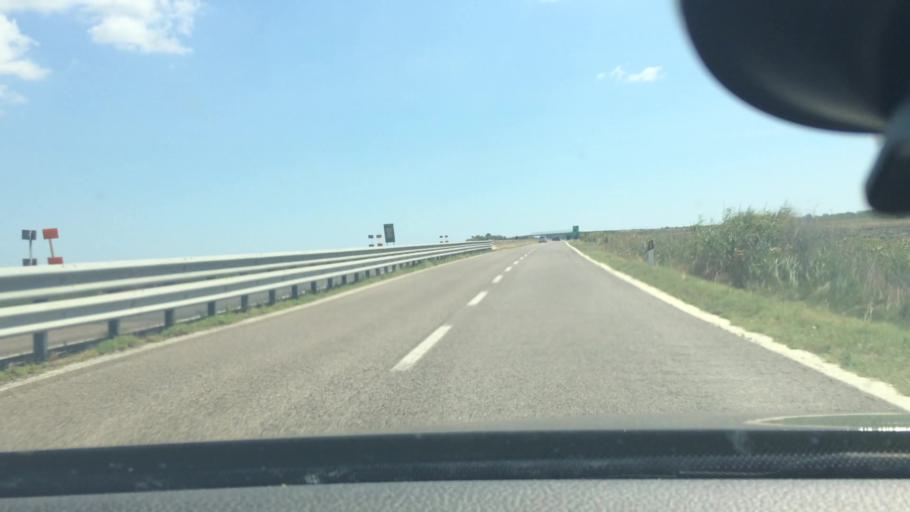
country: IT
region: Emilia-Romagna
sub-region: Provincia di Ferrara
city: Ostellato
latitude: 44.7557
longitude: 11.9731
